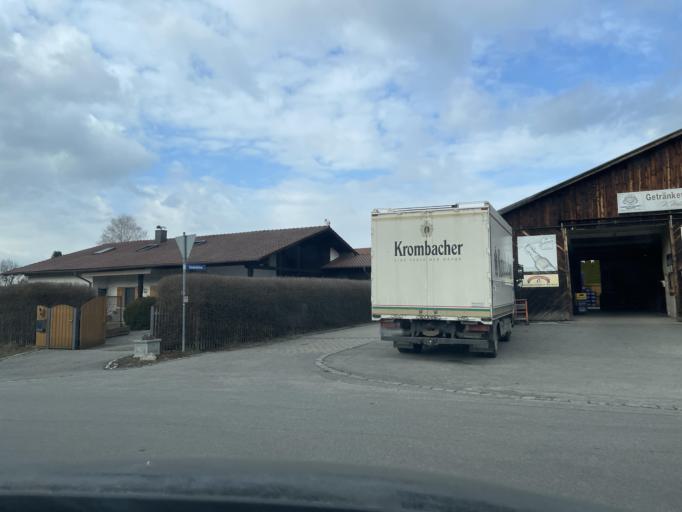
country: DE
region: Bavaria
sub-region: Lower Bavaria
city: Viechtach
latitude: 49.0832
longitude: 12.9053
